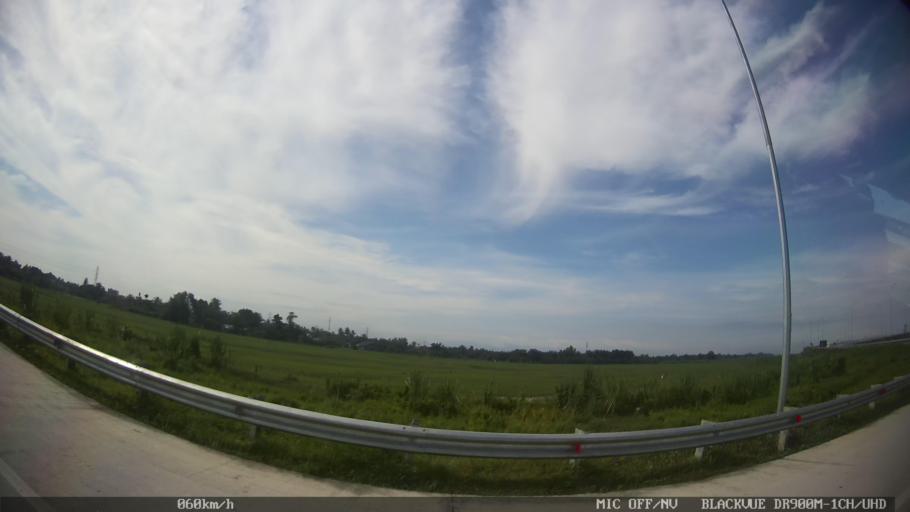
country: ID
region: North Sumatra
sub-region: Kabupaten Langkat
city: Stabat
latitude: 3.7135
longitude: 98.4991
